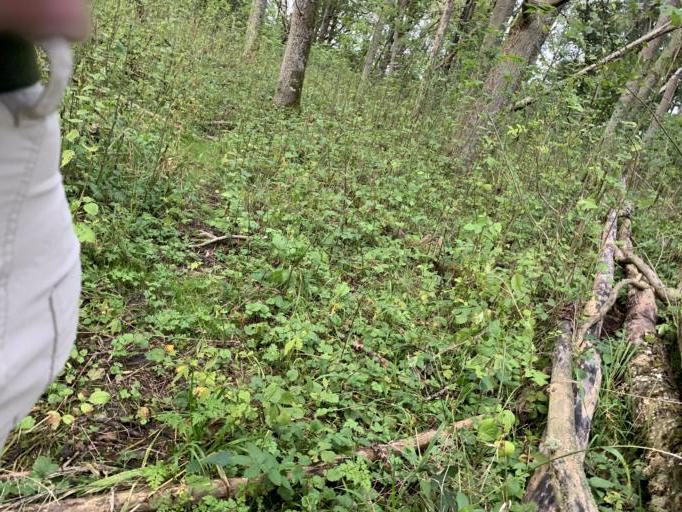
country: SE
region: Soedermanland
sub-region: Eskilstuna Kommun
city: Kvicksund
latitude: 59.4647
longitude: 16.2210
